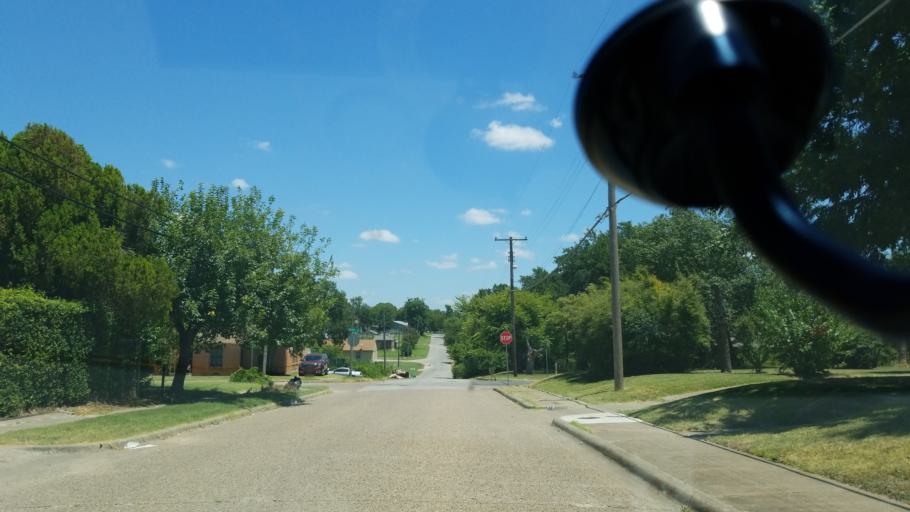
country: US
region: Texas
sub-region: Dallas County
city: Cockrell Hill
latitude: 32.6993
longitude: -96.8126
